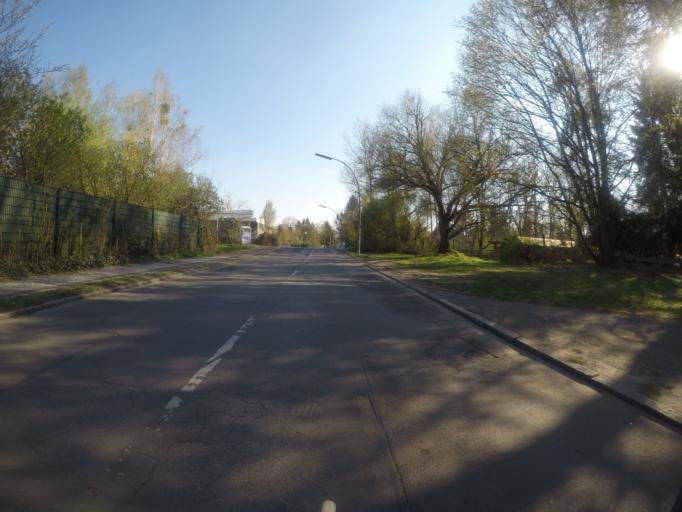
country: DE
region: Berlin
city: Zehlendorf Bezirk
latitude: 52.4267
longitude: 13.2434
